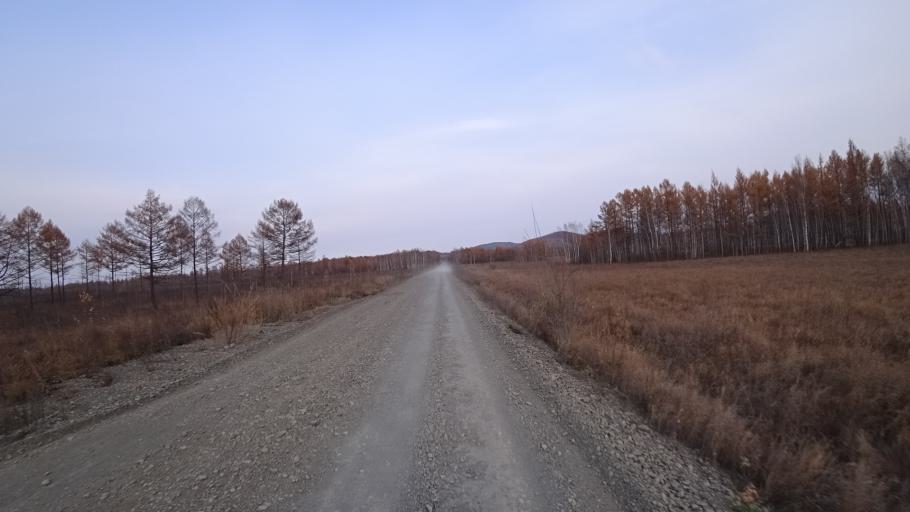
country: RU
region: Khabarovsk Krai
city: Amursk
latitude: 50.0102
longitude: 136.3950
